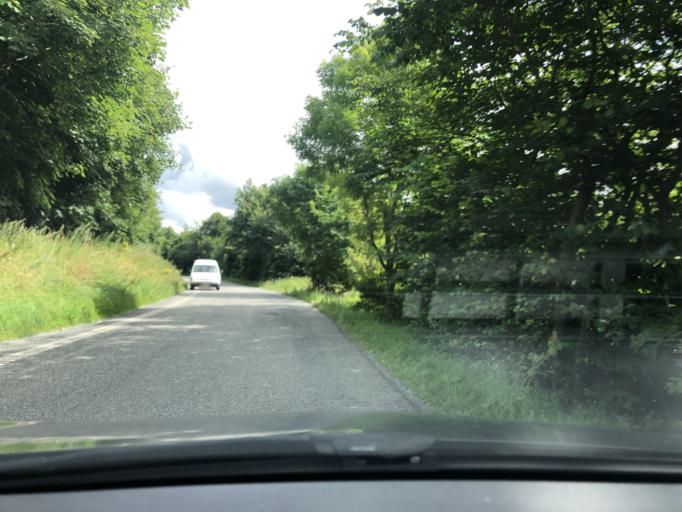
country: DK
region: South Denmark
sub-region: Vejle Kommune
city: Jelling
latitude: 55.6979
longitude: 9.4455
